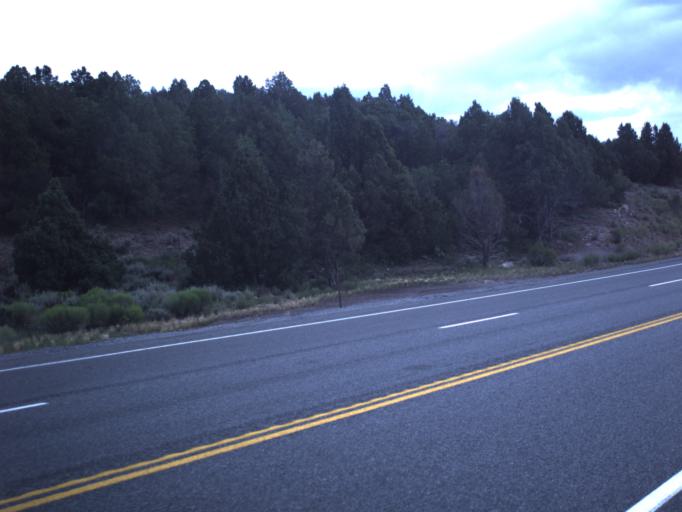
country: US
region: Utah
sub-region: Garfield County
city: Panguitch
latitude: 38.0262
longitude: -112.5315
